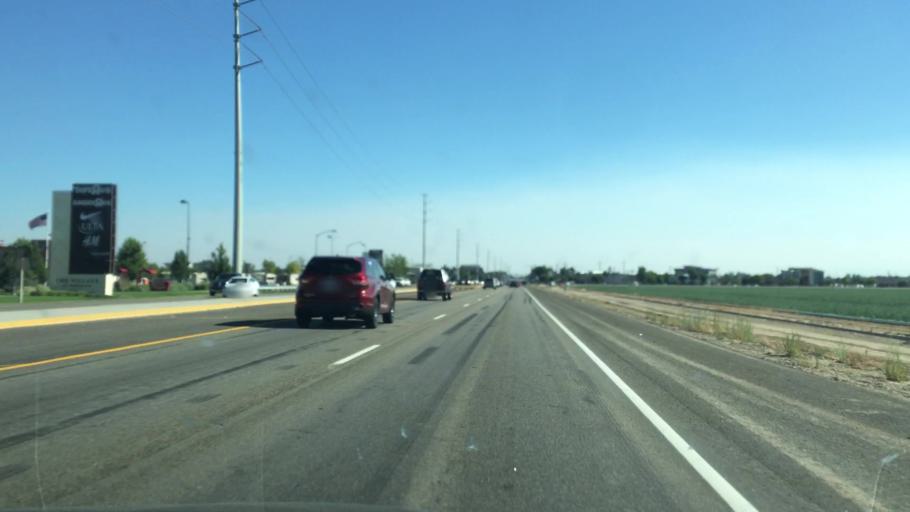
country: US
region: Idaho
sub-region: Ada County
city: Meridian
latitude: 43.6245
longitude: -116.3546
